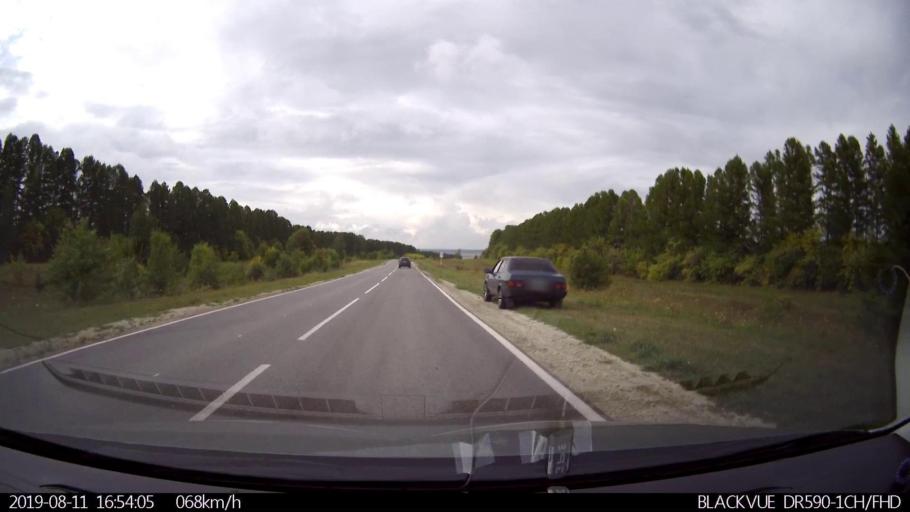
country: RU
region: Ulyanovsk
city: Mayna
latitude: 54.2691
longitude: 47.6674
